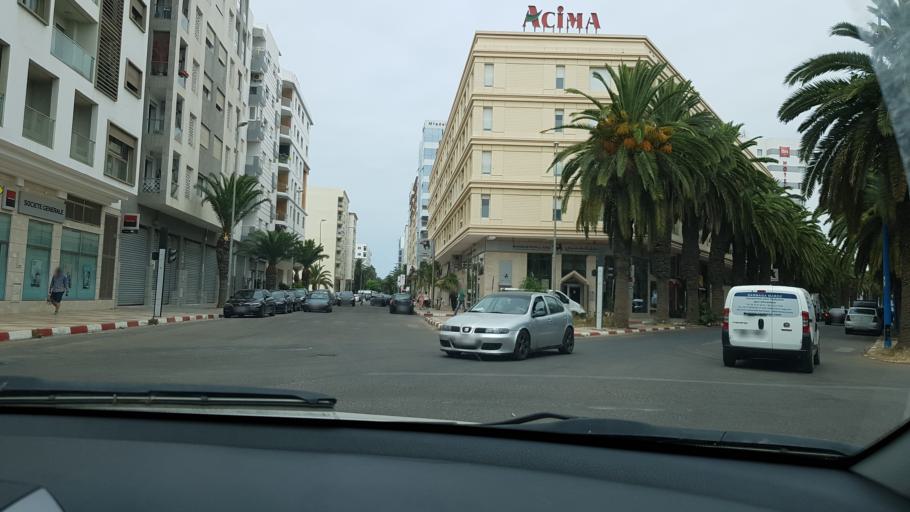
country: MA
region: Grand Casablanca
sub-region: Mohammedia
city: Mohammedia
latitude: 33.7033
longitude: -7.3980
